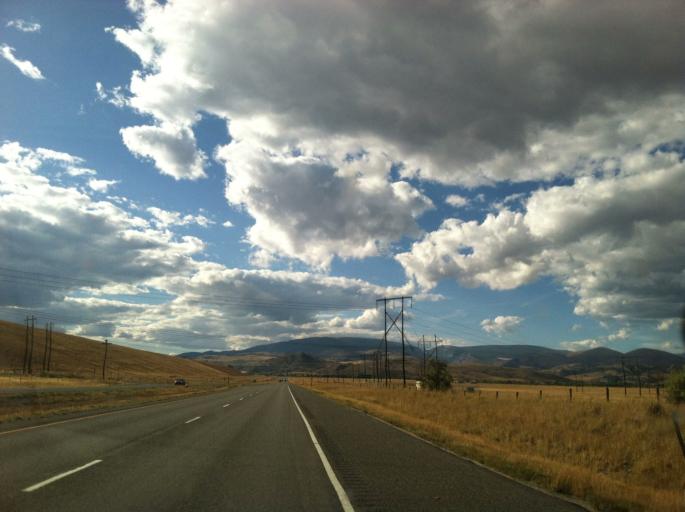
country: US
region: Montana
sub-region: Deer Lodge County
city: Anaconda
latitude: 46.1183
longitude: -112.8736
